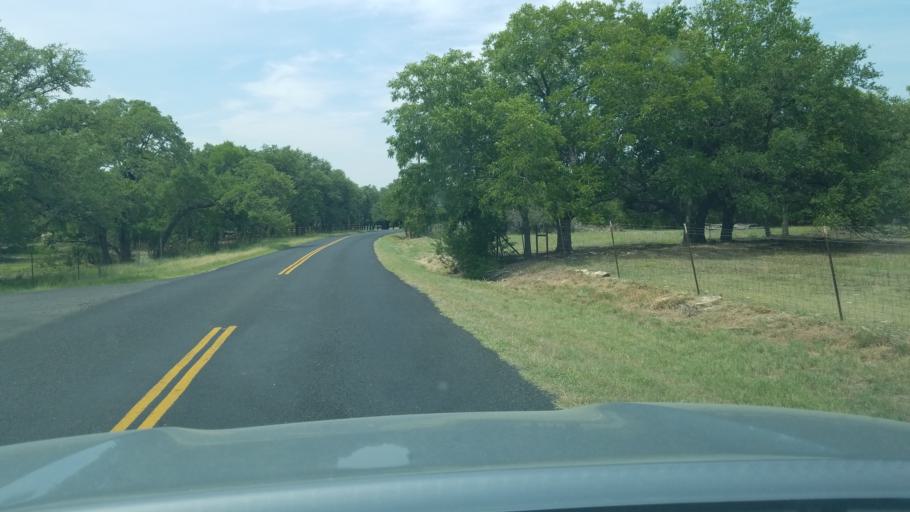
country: US
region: Texas
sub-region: Comal County
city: Bulverde
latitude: 29.7728
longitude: -98.4486
